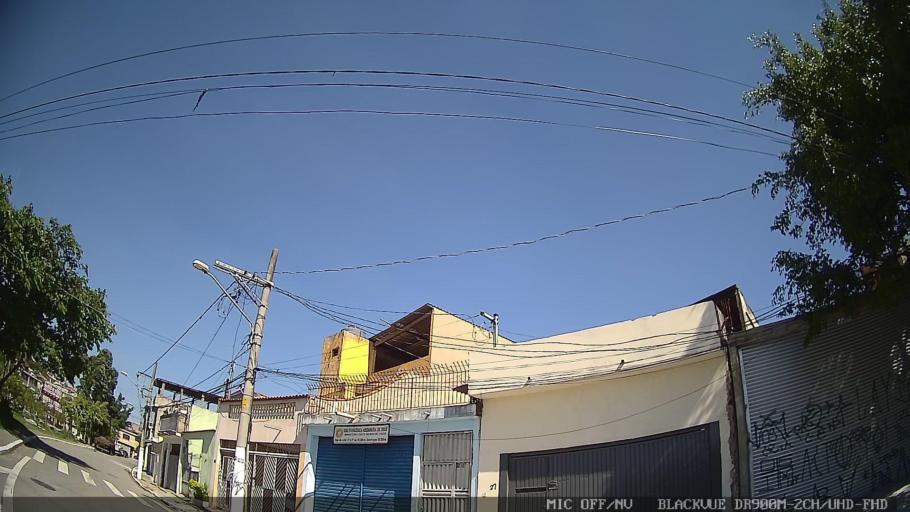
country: BR
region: Sao Paulo
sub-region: Sao Caetano Do Sul
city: Sao Caetano do Sul
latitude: -23.6052
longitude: -46.4869
